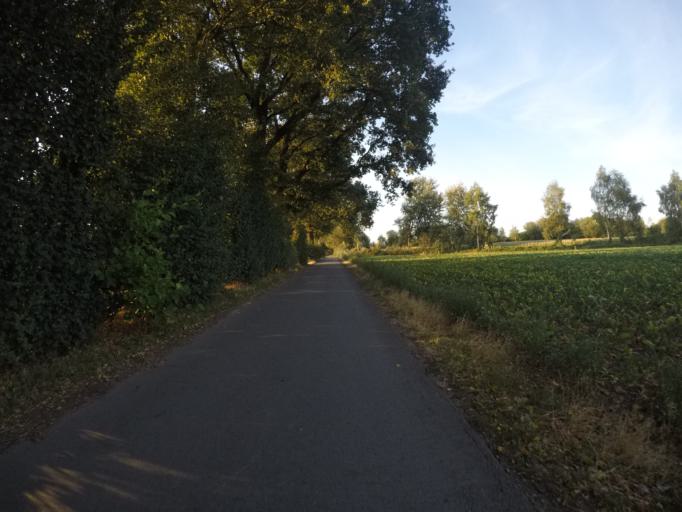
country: DE
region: North Rhine-Westphalia
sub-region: Regierungsbezirk Munster
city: Isselburg
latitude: 51.8539
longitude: 6.4860
